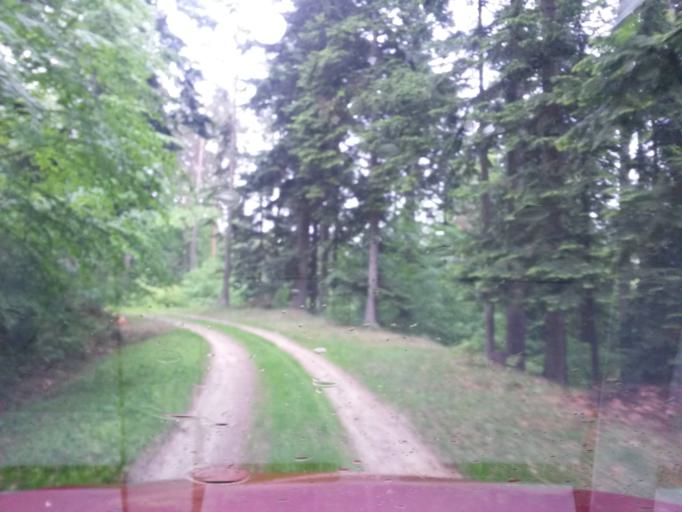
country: SK
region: Kosicky
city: Medzev
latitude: 48.7821
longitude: 20.7874
